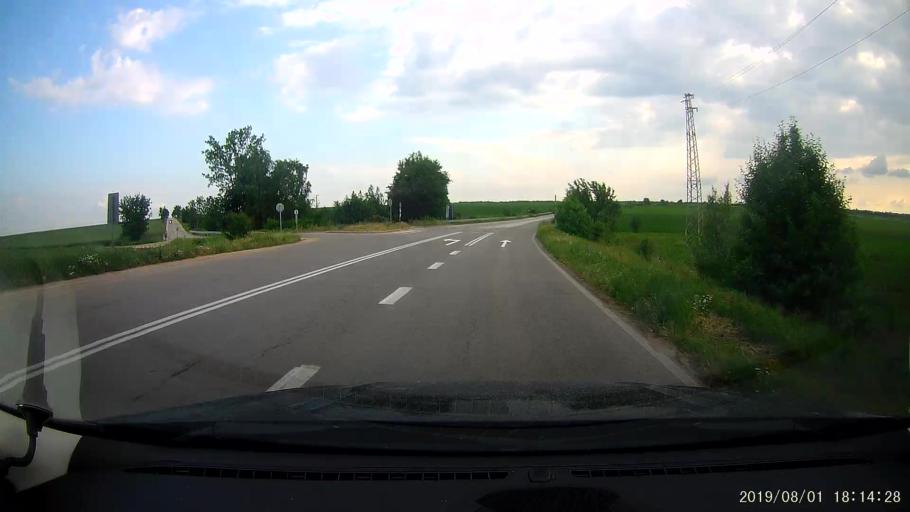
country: BG
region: Silistra
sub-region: Obshtina Dulovo
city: Dulovo
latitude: 43.7683
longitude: 27.1251
